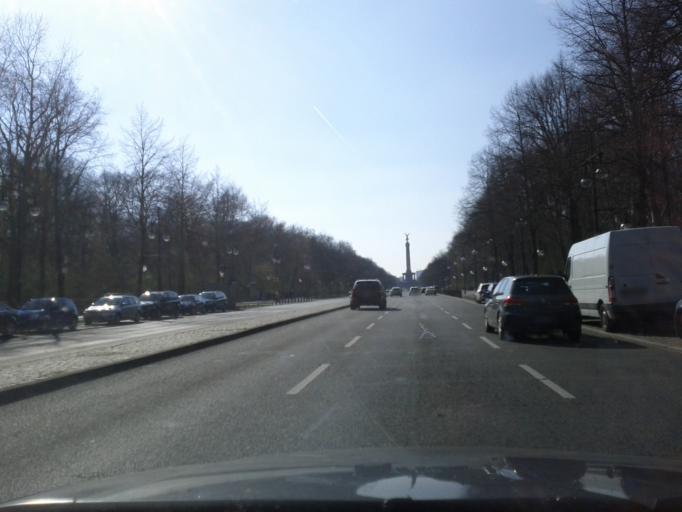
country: DE
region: Berlin
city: Tiergarten Bezirk
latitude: 52.5152
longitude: 13.3614
